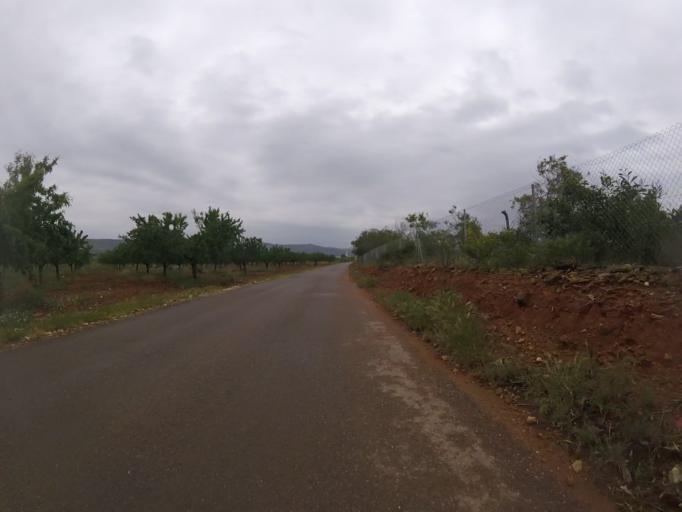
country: ES
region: Valencia
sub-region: Provincia de Castello
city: Alcala de Xivert
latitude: 40.2842
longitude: 0.2281
